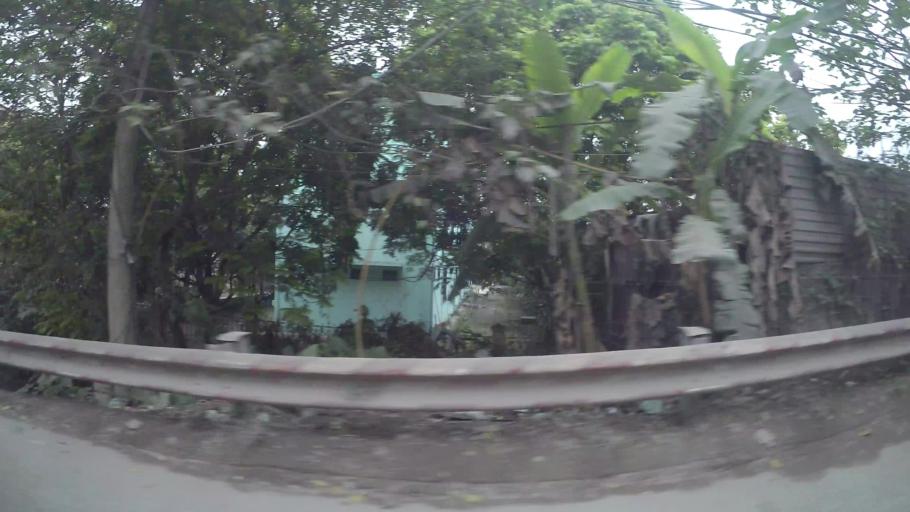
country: VN
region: Hung Yen
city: Van Giang
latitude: 20.9790
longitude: 105.8908
